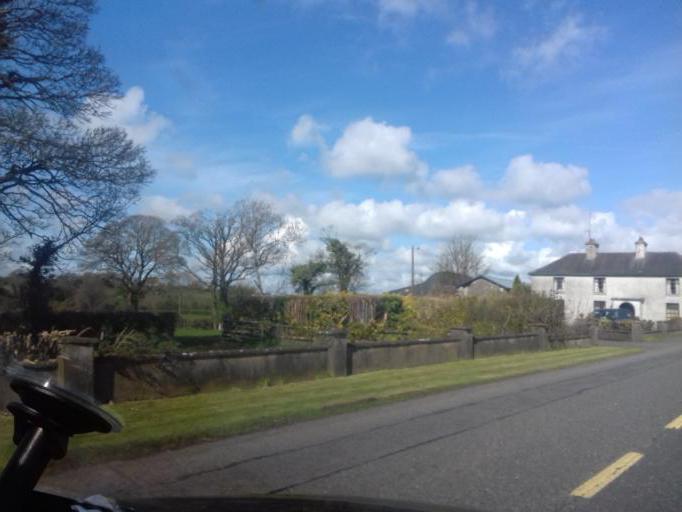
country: IE
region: Ulster
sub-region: An Cabhan
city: Mullagh
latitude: 53.7784
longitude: -7.0067
